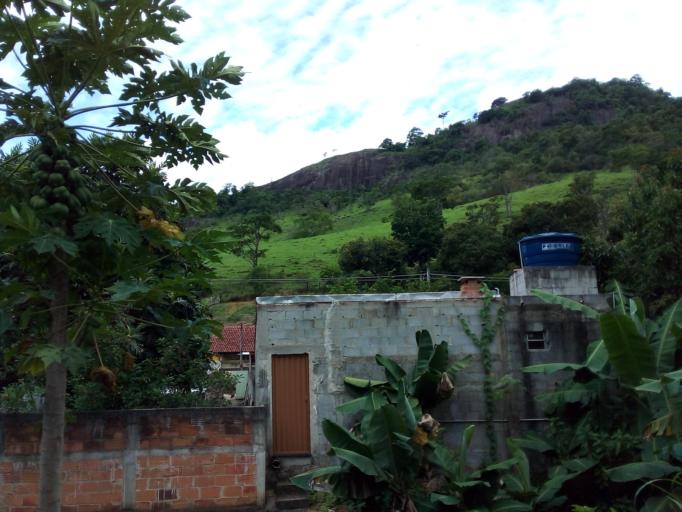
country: BR
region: Espirito Santo
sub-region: Joao Neiva
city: Joao Neiva
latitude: -19.7454
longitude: -40.3657
